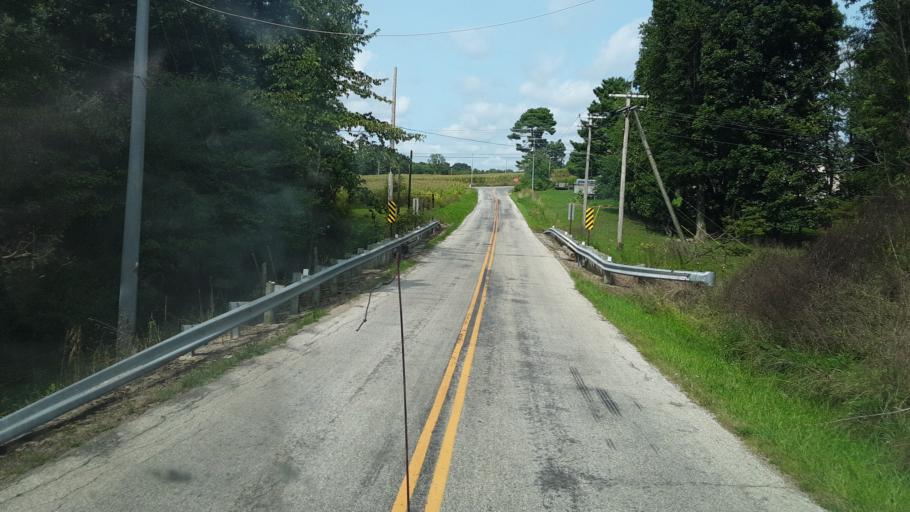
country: US
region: Ohio
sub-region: Ashland County
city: Loudonville
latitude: 40.5931
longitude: -82.3450
